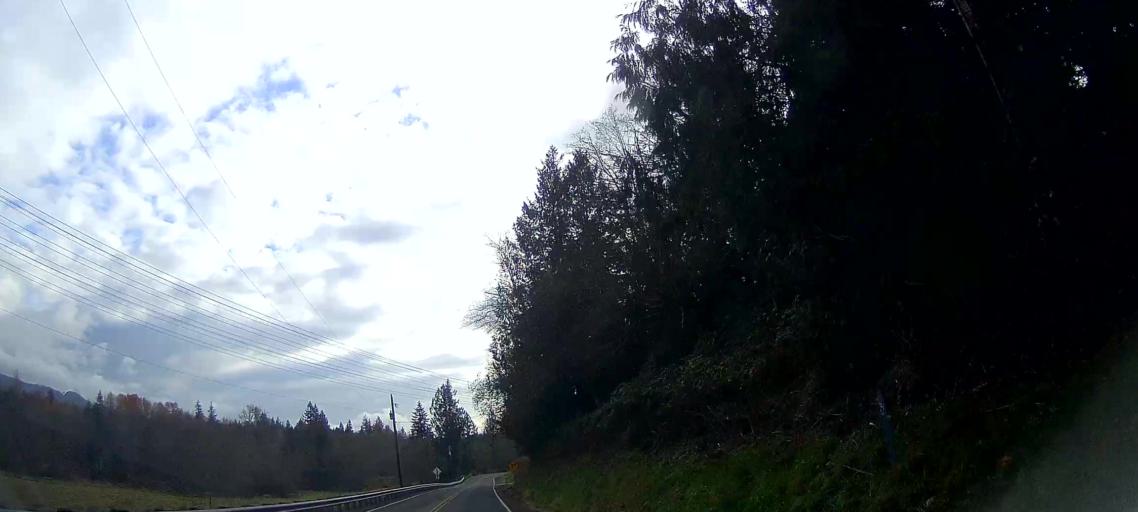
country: US
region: Washington
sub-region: Skagit County
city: Big Lake
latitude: 48.4085
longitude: -122.2144
